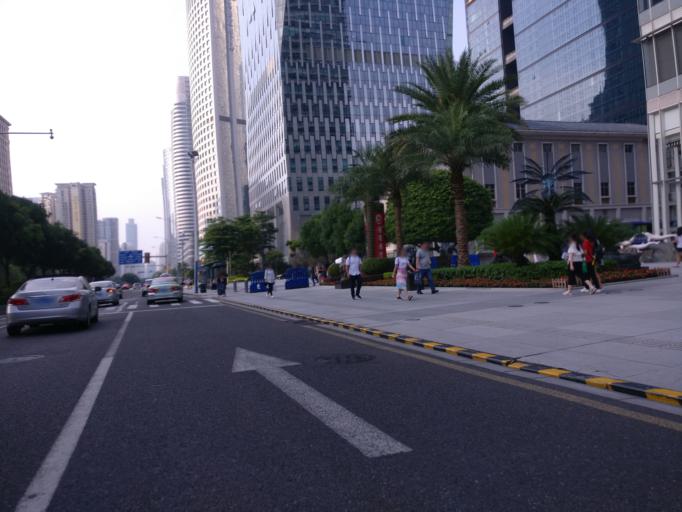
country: CN
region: Guangdong
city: Wushan
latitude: 23.1199
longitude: 113.3160
